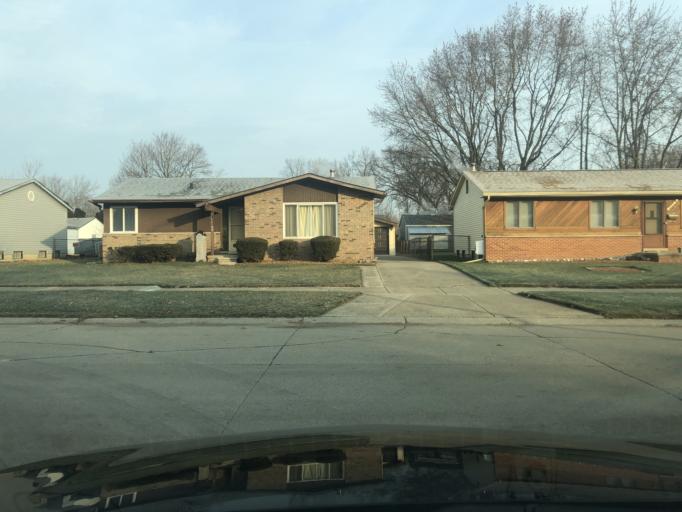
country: US
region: Michigan
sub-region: Wayne County
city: Romulus
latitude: 42.1904
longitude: -83.3325
